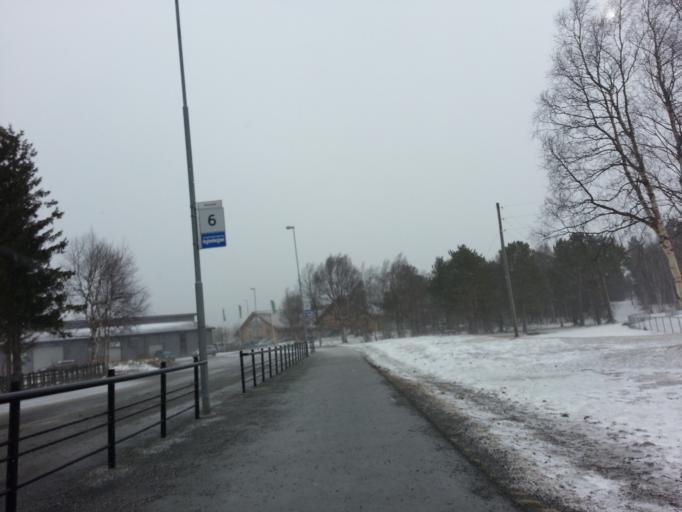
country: NO
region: Sor-Trondelag
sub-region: Oppdal
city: Oppdal
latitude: 62.5940
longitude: 9.6849
